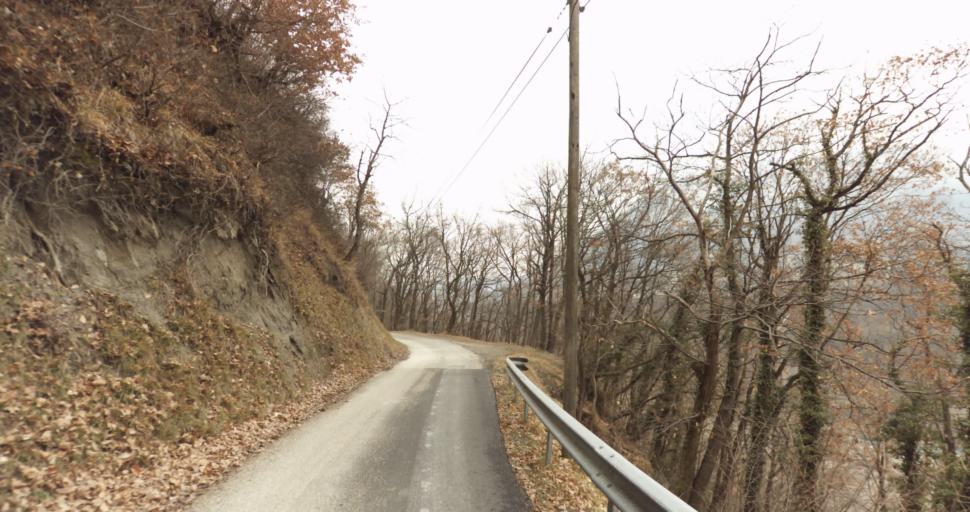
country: FR
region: Rhone-Alpes
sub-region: Departement de l'Isere
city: Saint-Georges-de-Commiers
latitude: 45.0324
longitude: 5.6904
